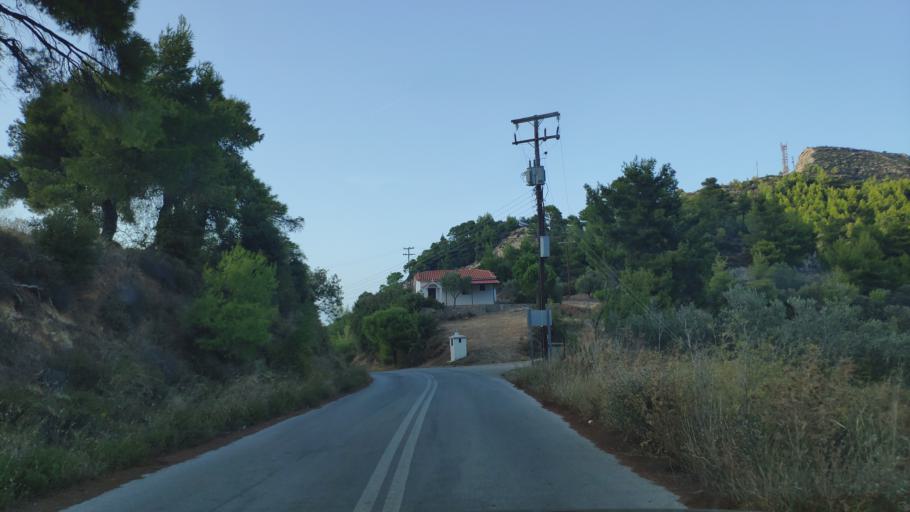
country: GR
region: West Greece
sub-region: Nomos Achaias
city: Aiyira
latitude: 38.0979
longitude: 22.4080
